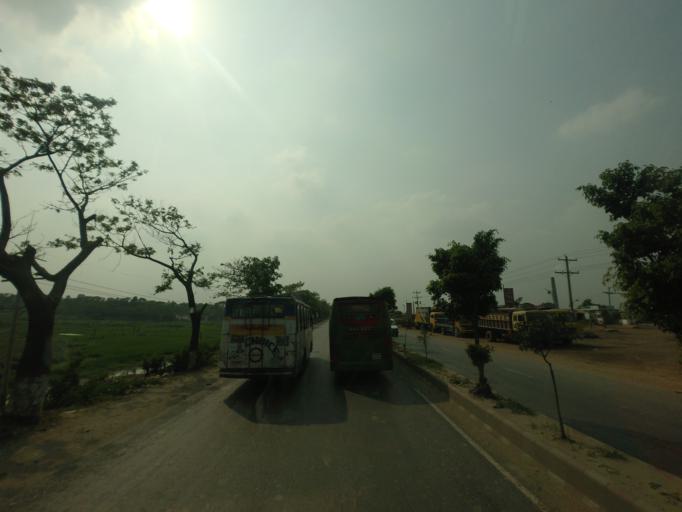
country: BD
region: Dhaka
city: Azimpur
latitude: 23.7909
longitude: 90.3089
